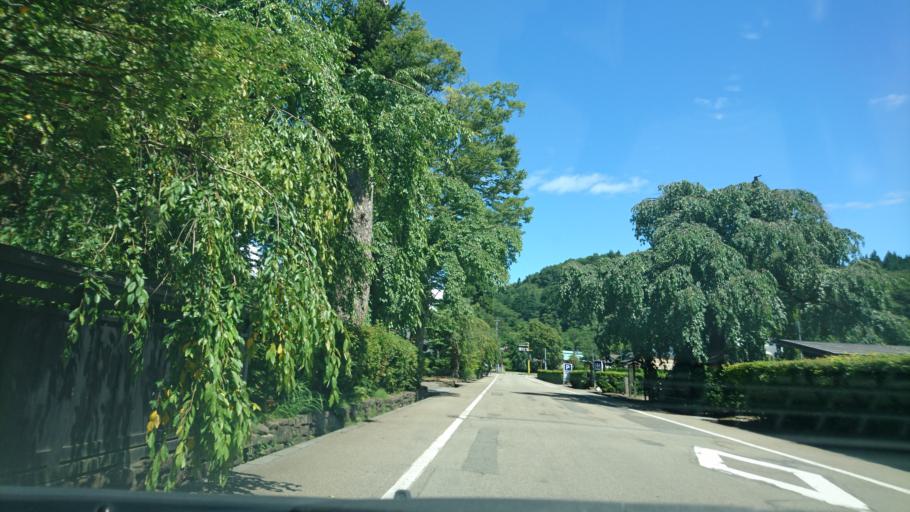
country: JP
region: Akita
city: Kakunodatemachi
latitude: 39.6012
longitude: 140.5613
